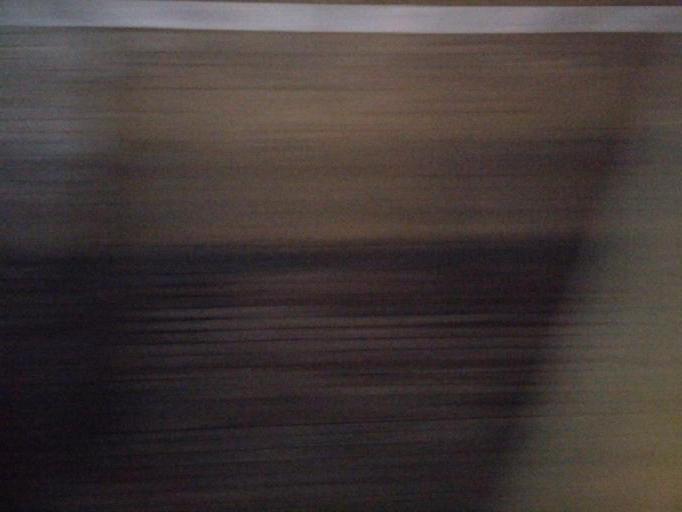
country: NO
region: Akershus
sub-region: Baerum
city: Lysaker
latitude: 59.9470
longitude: 10.6430
